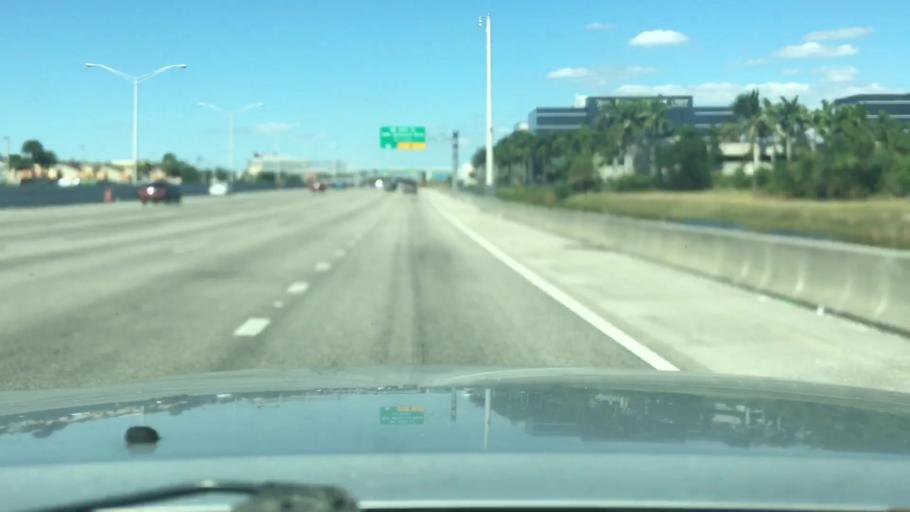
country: US
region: Florida
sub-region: Miami-Dade County
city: Flagami
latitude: 25.7886
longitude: -80.3209
